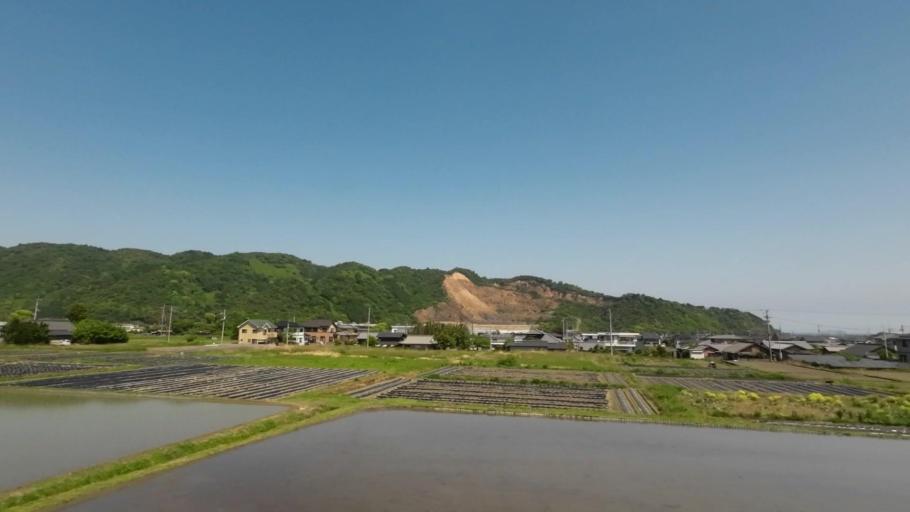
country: JP
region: Ehime
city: Niihama
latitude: 33.9569
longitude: 133.4194
